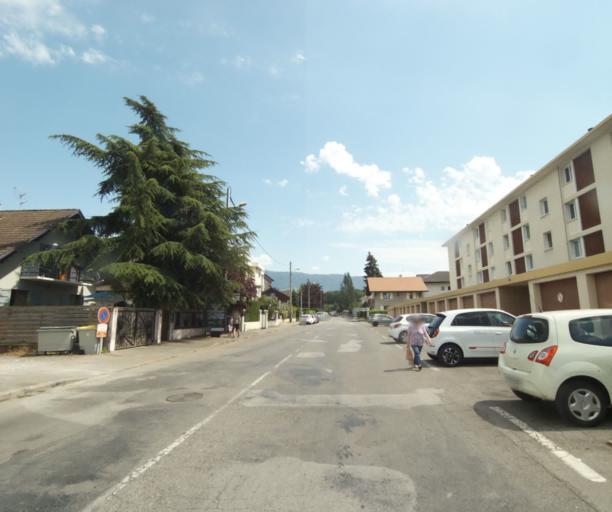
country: FR
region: Rhone-Alpes
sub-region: Departement de la Haute-Savoie
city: Thonon-les-Bains
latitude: 46.3641
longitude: 6.4641
